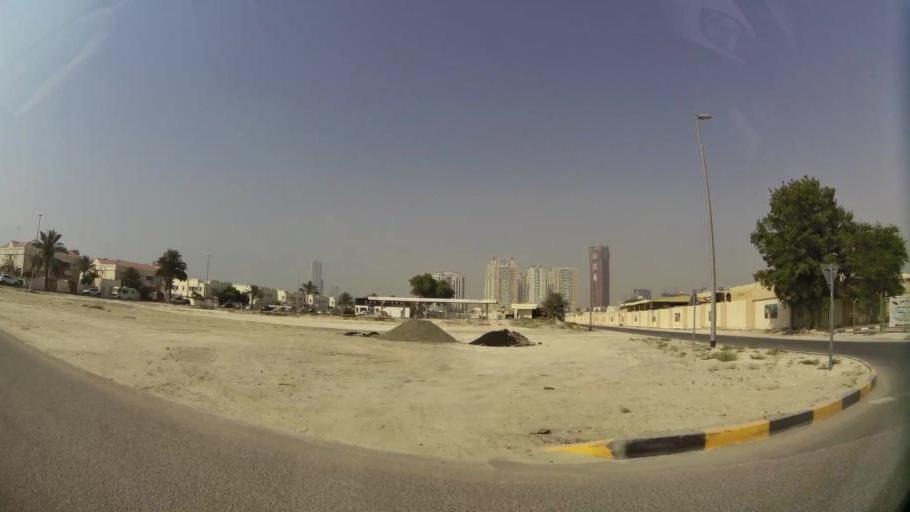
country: AE
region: Ajman
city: Ajman
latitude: 25.3892
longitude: 55.4218
